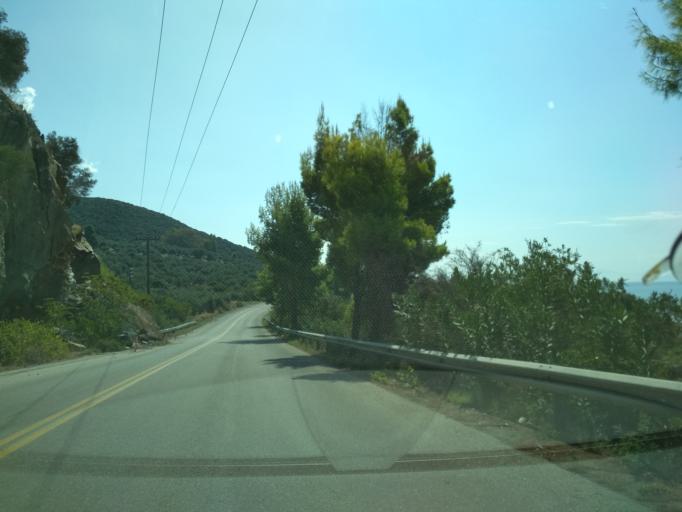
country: GR
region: Central Greece
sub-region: Nomos Evvoias
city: Roviai
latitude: 38.8439
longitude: 23.1678
